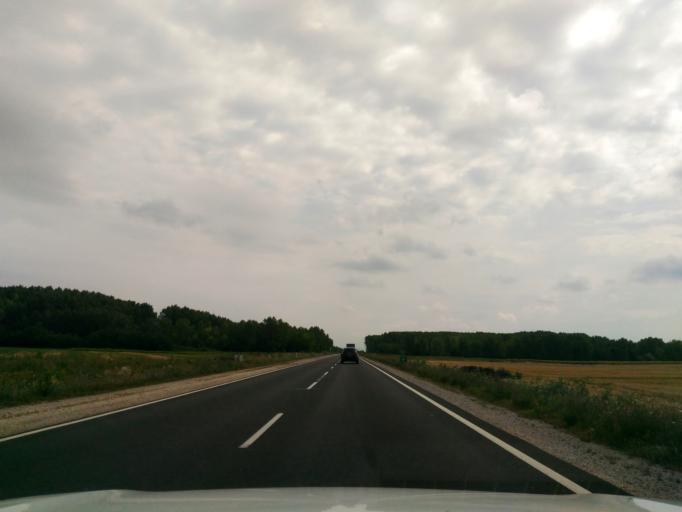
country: HU
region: Pest
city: Abony
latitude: 47.2050
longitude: 19.9577
